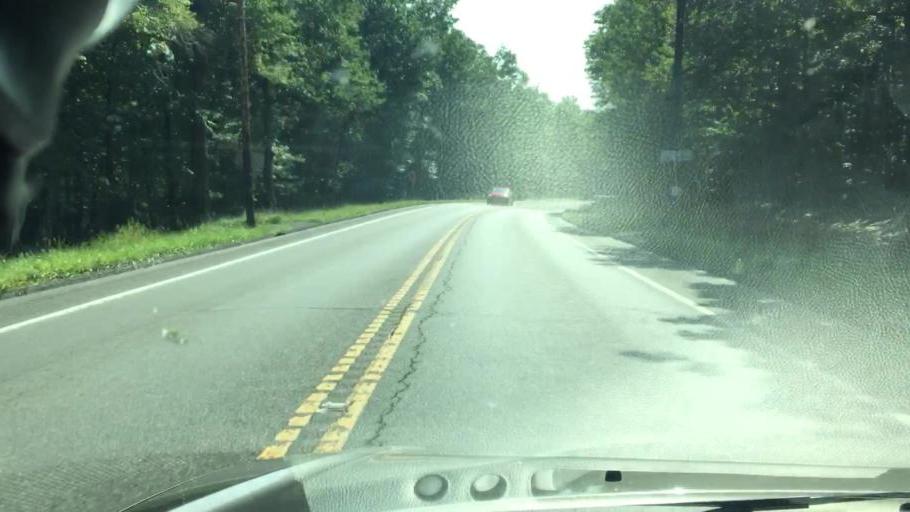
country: US
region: Pennsylvania
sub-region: Carbon County
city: Jim Thorpe
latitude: 40.8896
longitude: -75.6981
